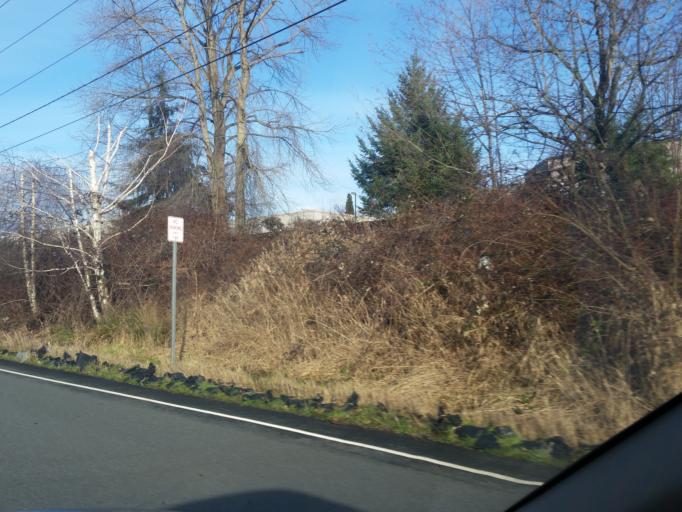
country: US
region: Washington
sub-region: King County
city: Woodinville
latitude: 47.7704
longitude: -122.1540
